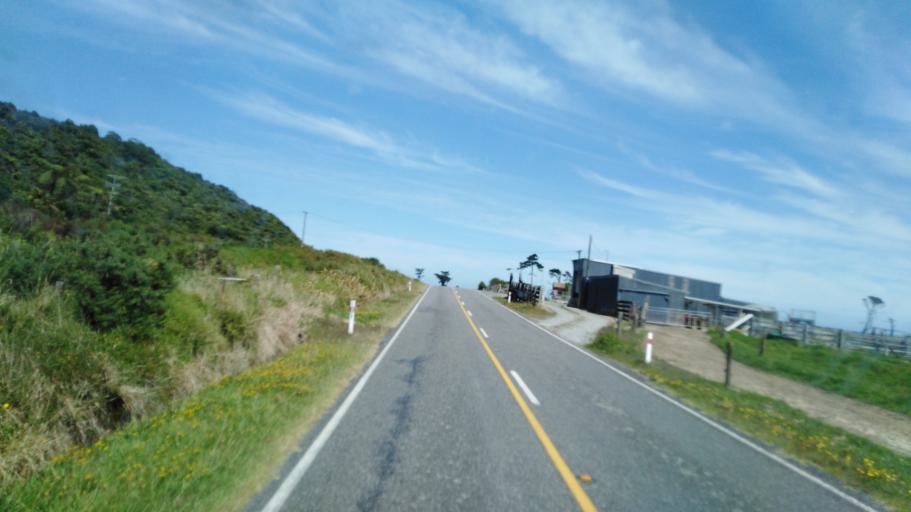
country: NZ
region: West Coast
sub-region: Buller District
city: Westport
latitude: -41.5333
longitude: 171.9370
